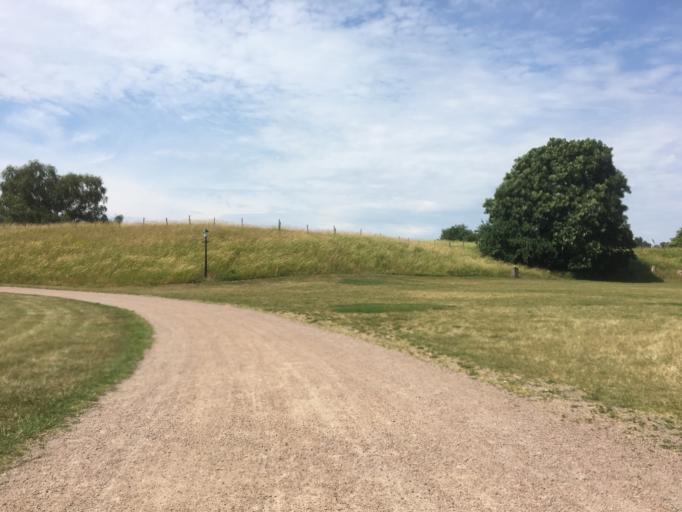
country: SE
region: Skane
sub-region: Landskrona
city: Landskrona
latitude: 55.8742
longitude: 12.8235
